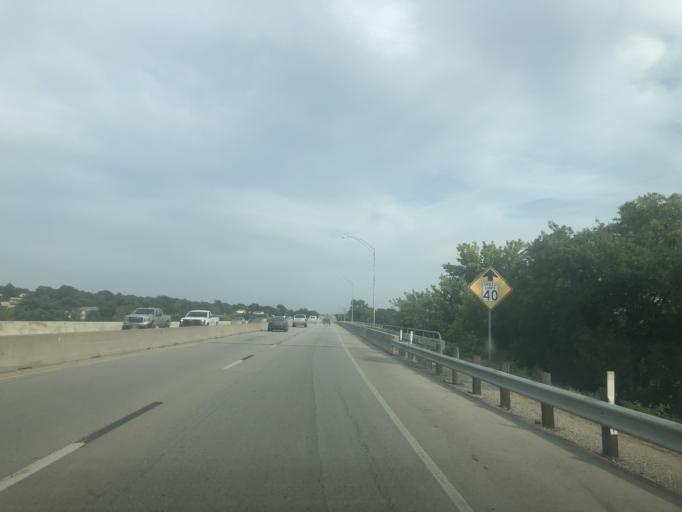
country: US
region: Texas
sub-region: Tarrant County
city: Lake Worth
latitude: 32.8220
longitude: -97.4476
